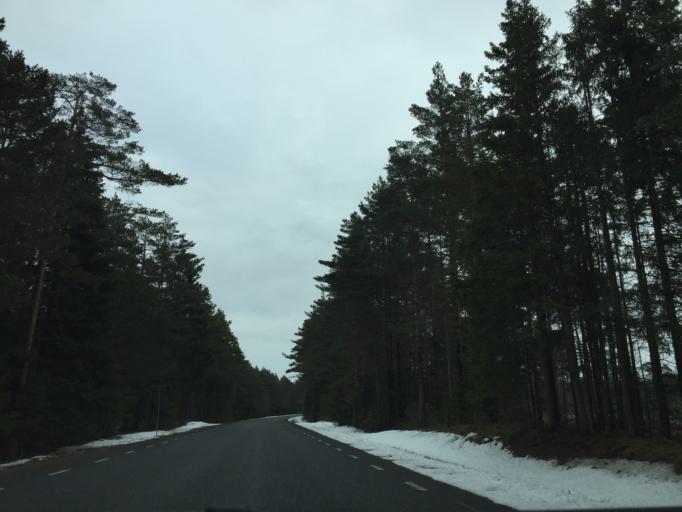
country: EE
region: Saare
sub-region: Kuressaare linn
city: Kuressaare
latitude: 58.4275
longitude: 22.1845
